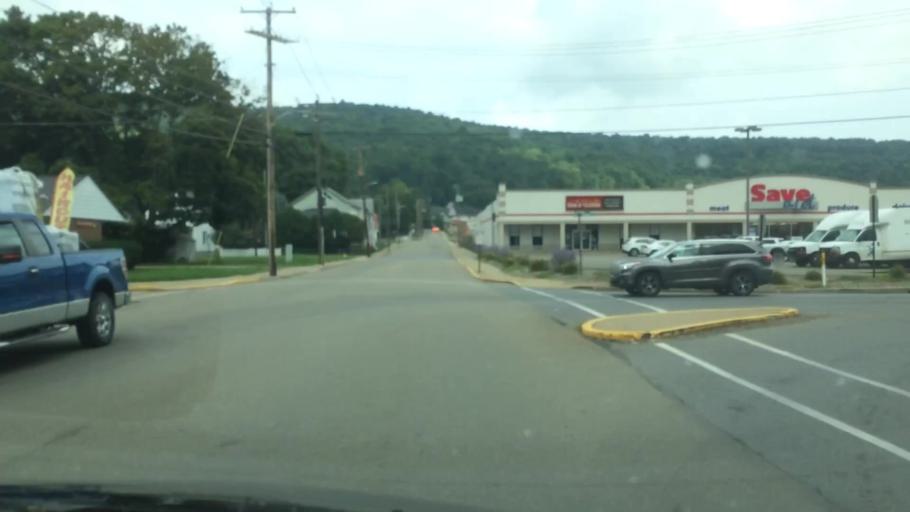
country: US
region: Pennsylvania
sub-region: McKean County
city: Bradford
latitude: 41.9578
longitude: -78.6451
